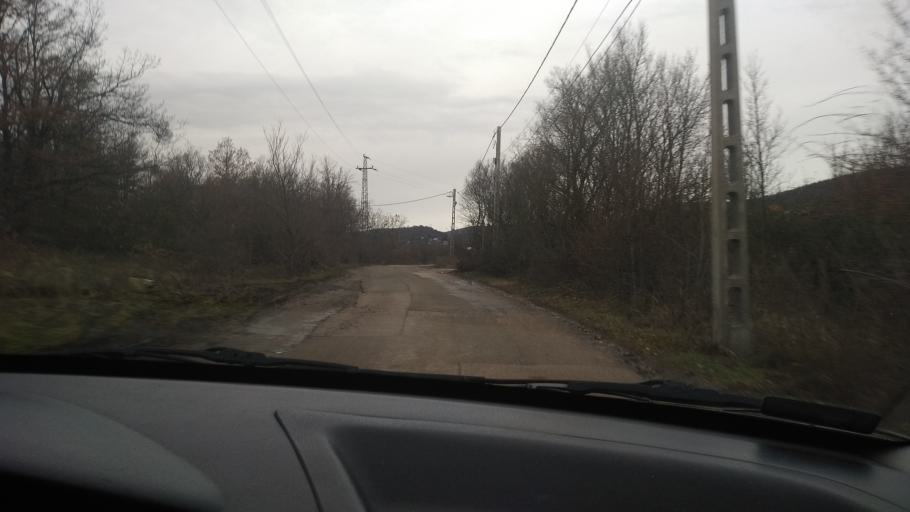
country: HU
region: Pest
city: Szentendre
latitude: 47.6930
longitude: 19.0538
